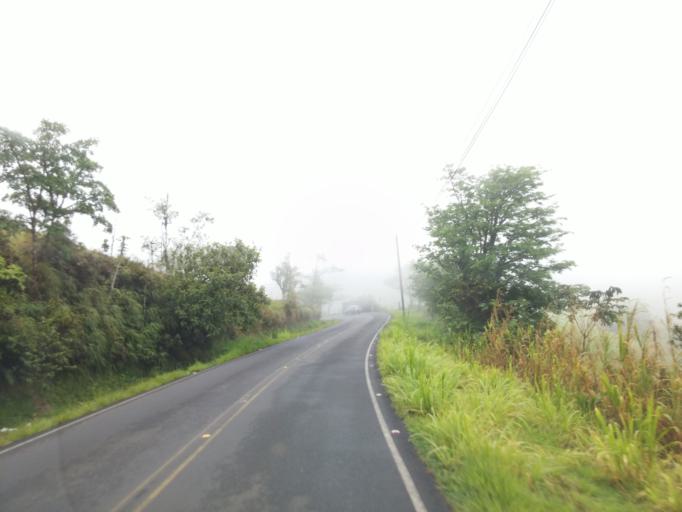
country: CR
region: Alajuela
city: San Ramon
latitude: 10.1618
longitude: -84.4930
